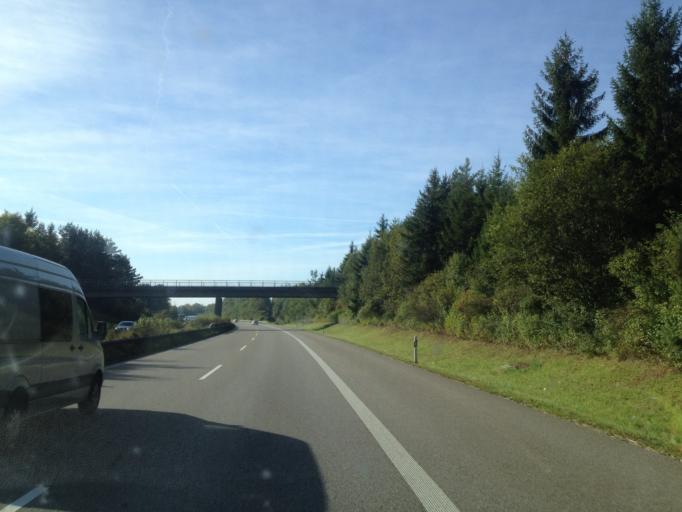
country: DE
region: Baden-Wuerttemberg
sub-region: Karlsruhe Region
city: Empfingen
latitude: 48.4128
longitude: 8.7271
